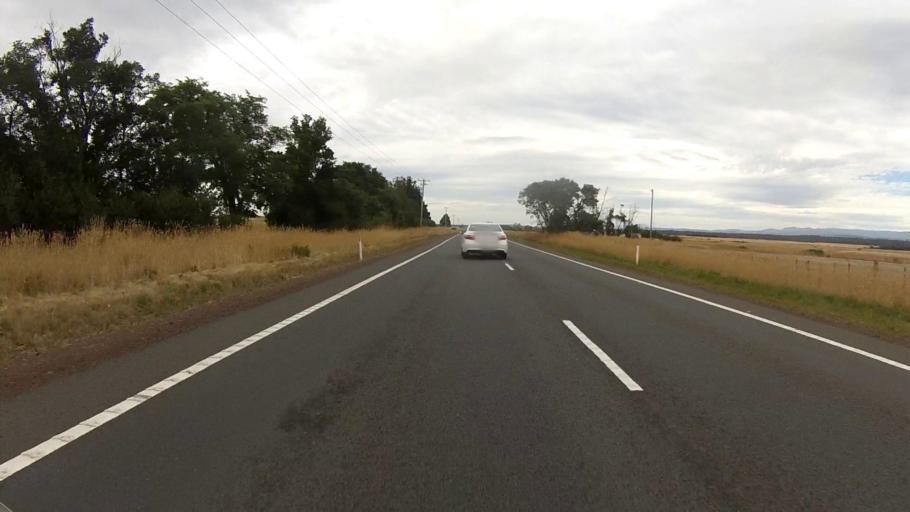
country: AU
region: Tasmania
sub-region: Northern Midlands
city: Evandale
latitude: -41.9023
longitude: 147.4770
